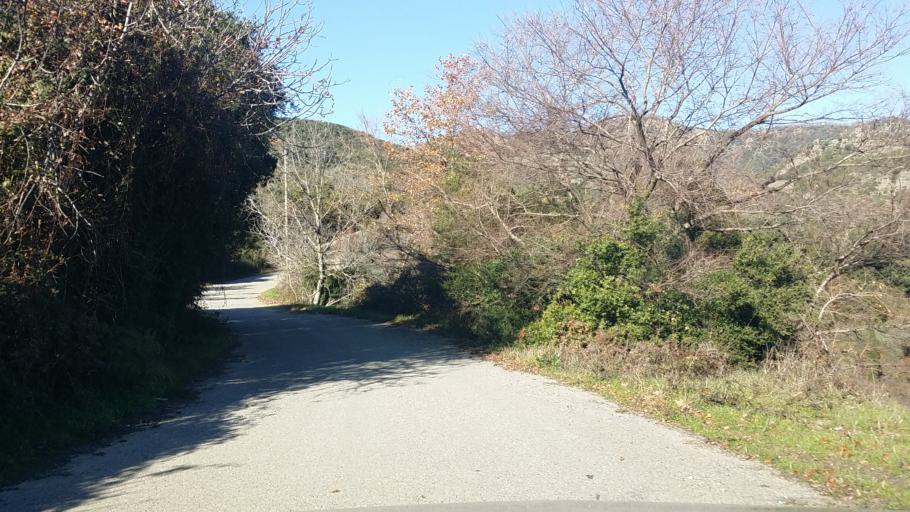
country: GR
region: West Greece
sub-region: Nomos Aitolias kai Akarnanias
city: Krikellos
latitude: 39.0038
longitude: 21.2420
